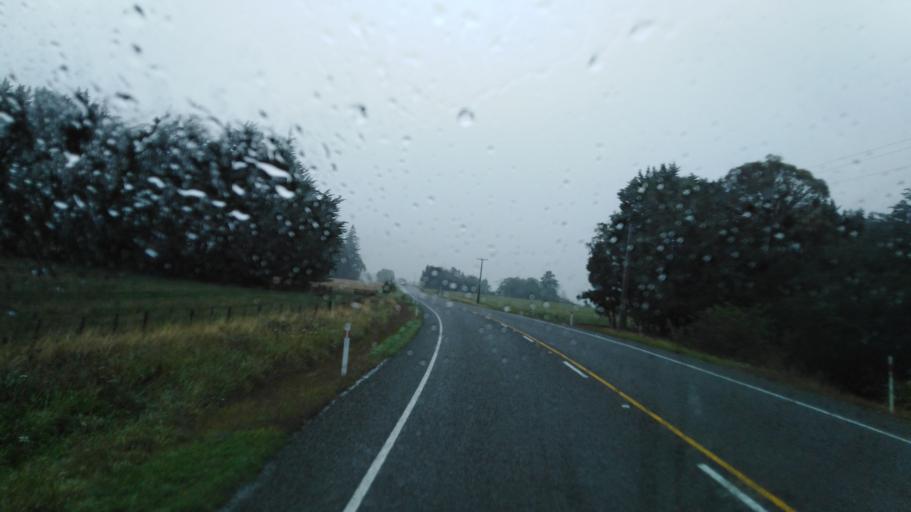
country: NZ
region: Marlborough
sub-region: Marlborough District
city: Blenheim
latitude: -41.3846
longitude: 173.7662
